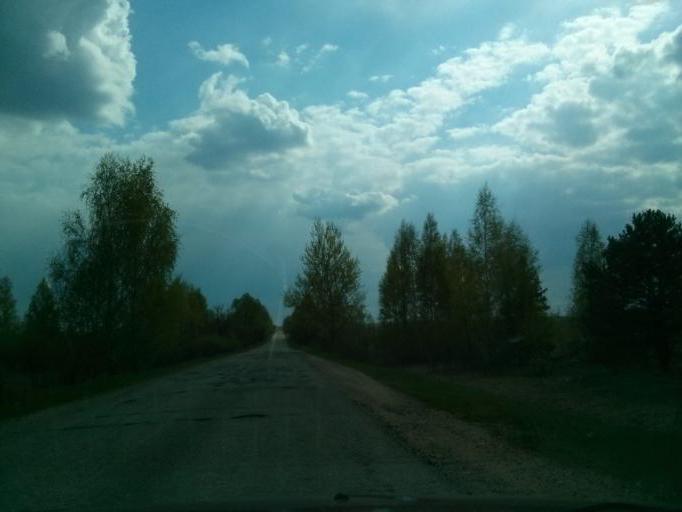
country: RU
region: Nizjnij Novgorod
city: Shimorskoye
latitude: 55.4441
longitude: 41.9779
